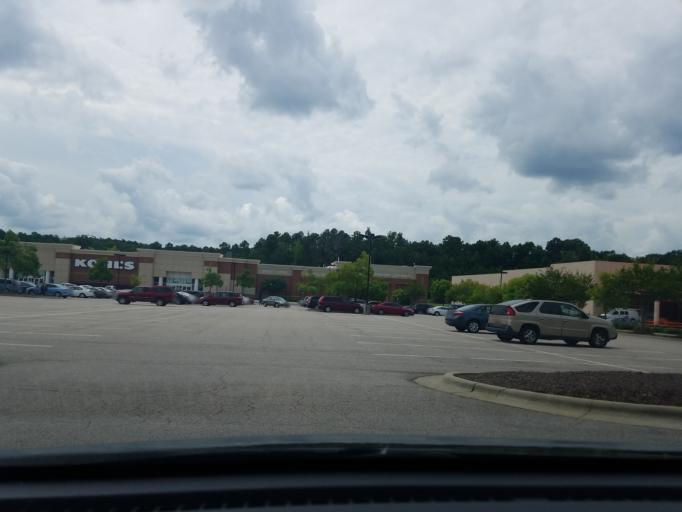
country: US
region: North Carolina
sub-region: Orange County
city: Chapel Hill
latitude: 35.9506
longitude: -78.9917
